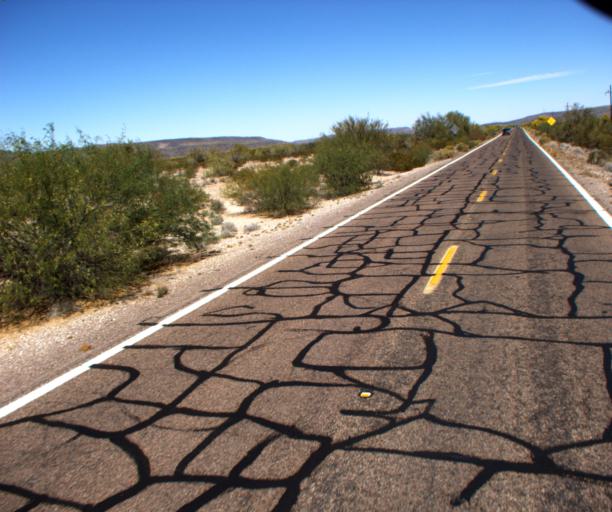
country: US
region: Arizona
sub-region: Pima County
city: Ajo
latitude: 32.4277
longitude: -112.8713
